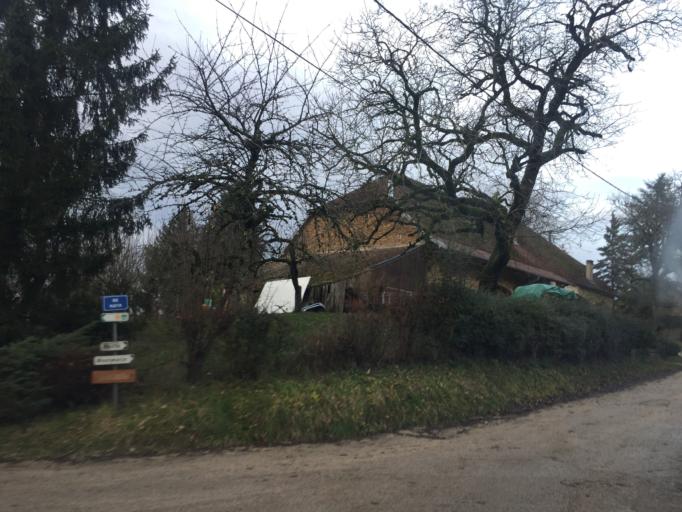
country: FR
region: Franche-Comte
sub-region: Departement du Jura
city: Mont-sous-Vaudrey
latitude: 46.9405
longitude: 5.6844
